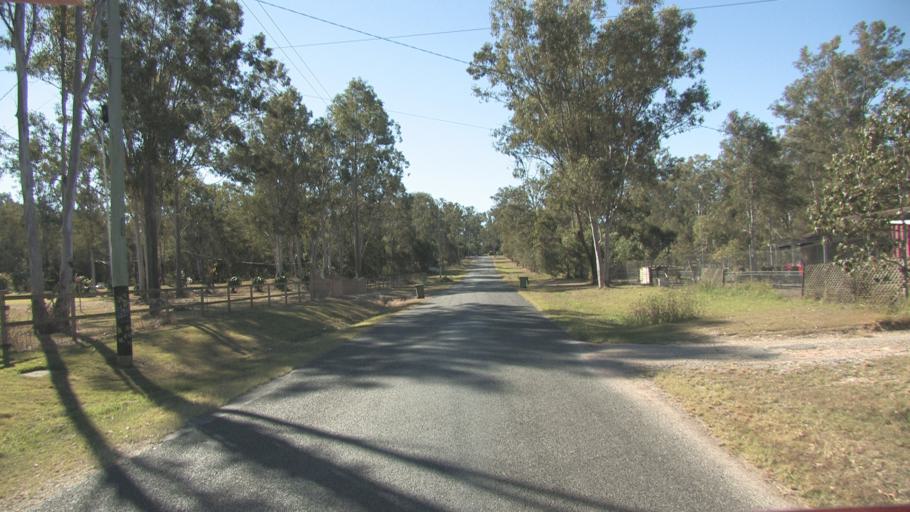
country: AU
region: Queensland
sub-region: Logan
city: Park Ridge South
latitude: -27.7237
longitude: 152.9910
